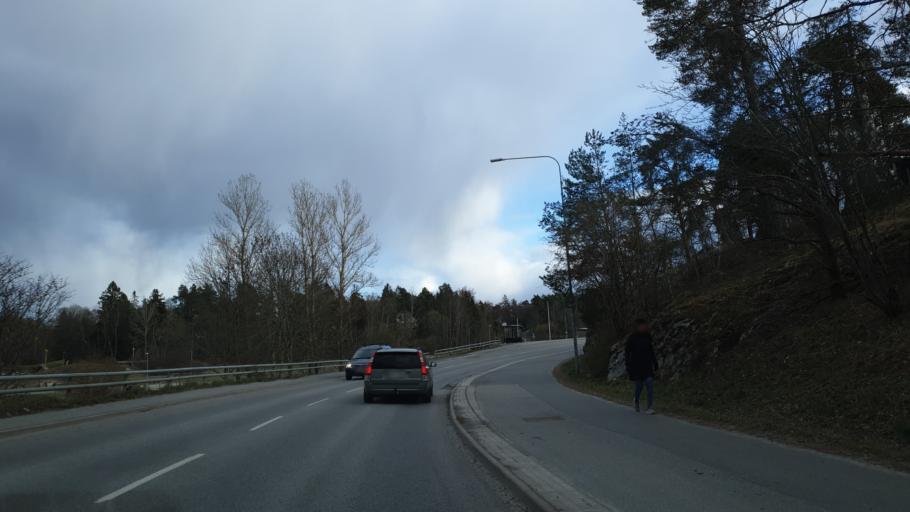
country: SE
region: Stockholm
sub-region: Lidingo
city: Lidingoe
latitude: 59.3736
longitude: 18.1324
